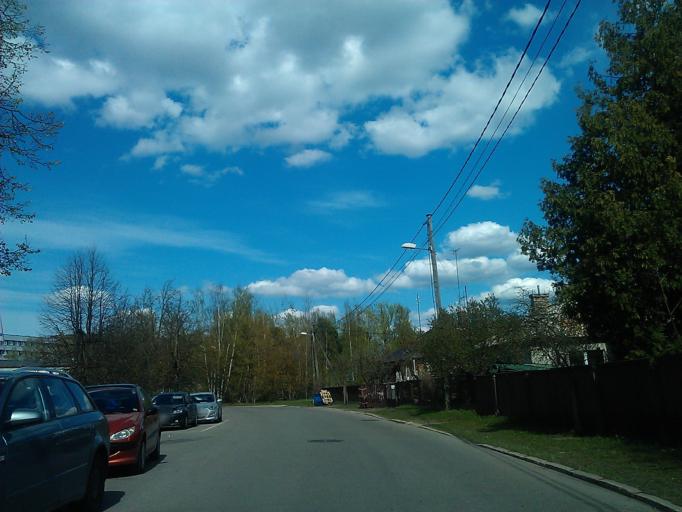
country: LV
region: Riga
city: Jaunciems
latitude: 56.9748
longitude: 24.1932
